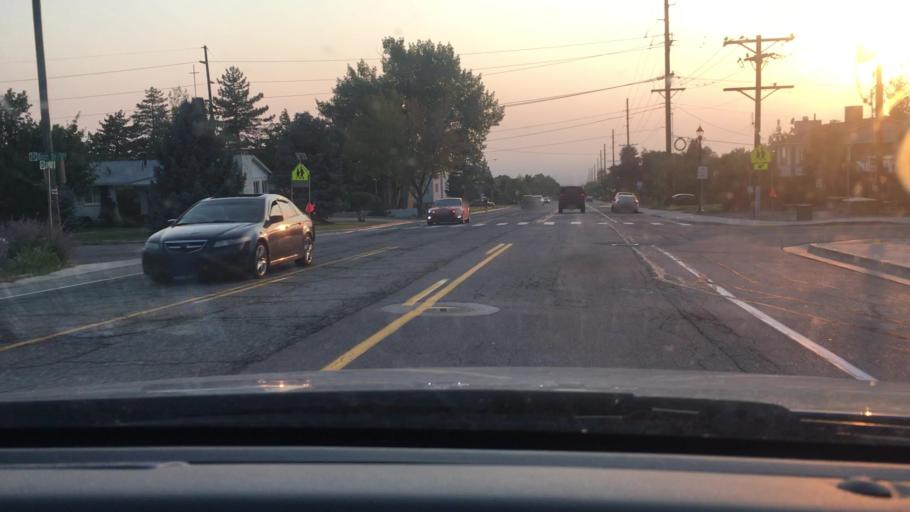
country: US
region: Utah
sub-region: Salt Lake County
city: Mount Olympus
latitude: 40.6870
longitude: -111.7998
